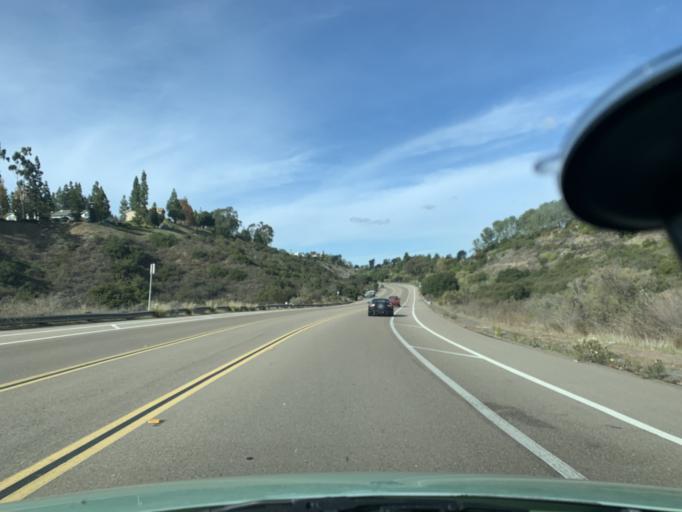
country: US
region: California
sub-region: San Diego County
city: San Diego
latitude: 32.8010
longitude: -117.1734
